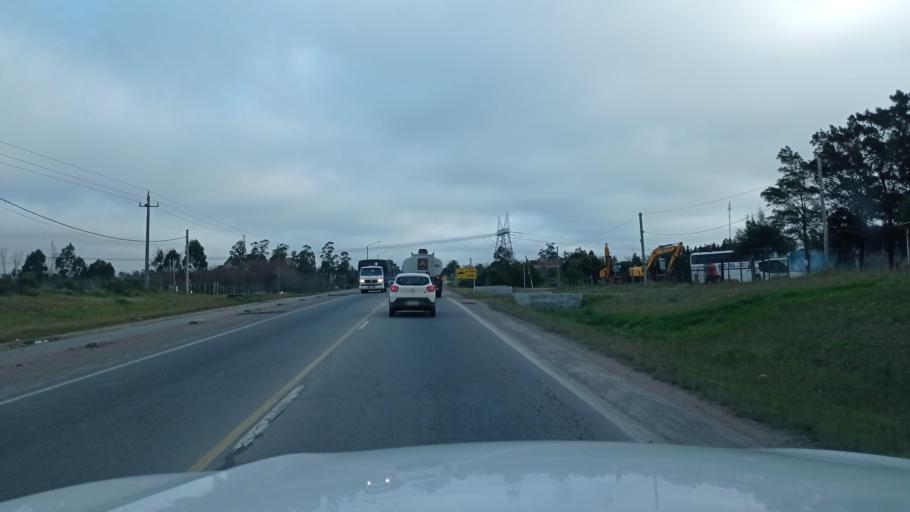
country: UY
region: Canelones
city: Toledo
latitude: -34.7705
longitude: -56.1256
